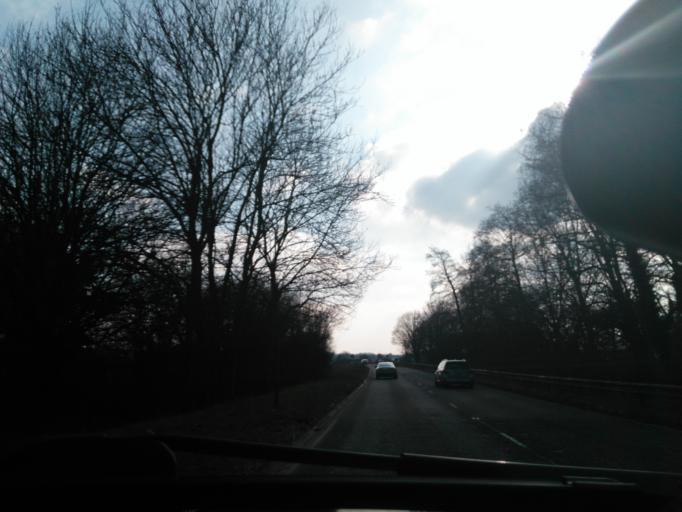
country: GB
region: England
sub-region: Wiltshire
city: Chippenham
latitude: 51.5047
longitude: -2.1256
